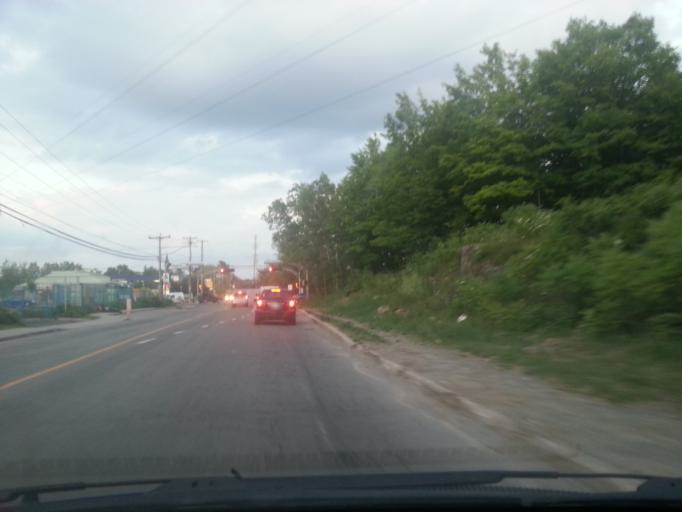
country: CA
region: Quebec
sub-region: Outaouais
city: Gatineau
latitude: 45.4929
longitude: -75.6425
